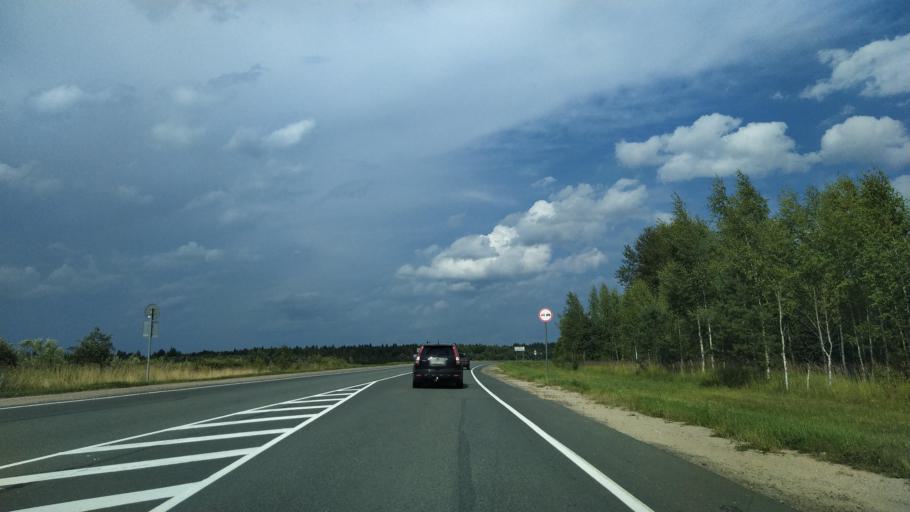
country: RU
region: Pskov
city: Porkhov
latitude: 57.8541
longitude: 29.5529
